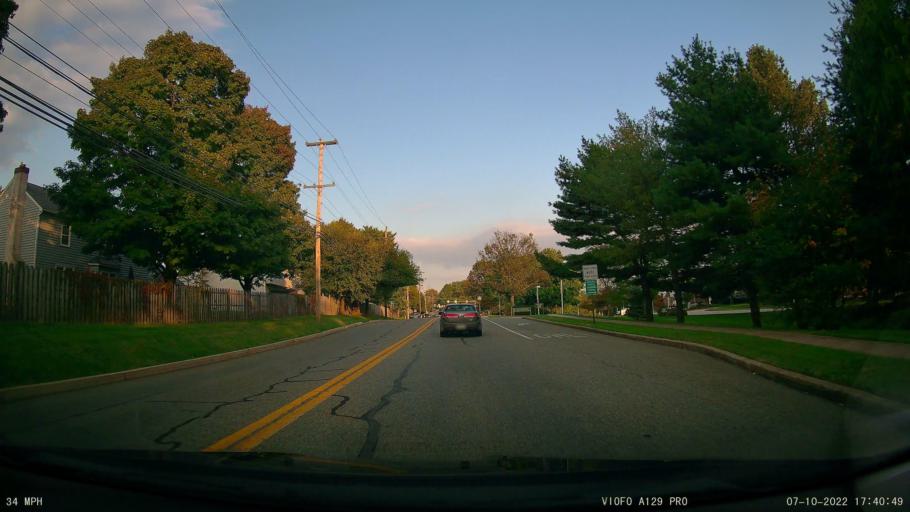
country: US
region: Pennsylvania
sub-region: Montgomery County
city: King of Prussia
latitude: 40.1027
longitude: -75.3731
